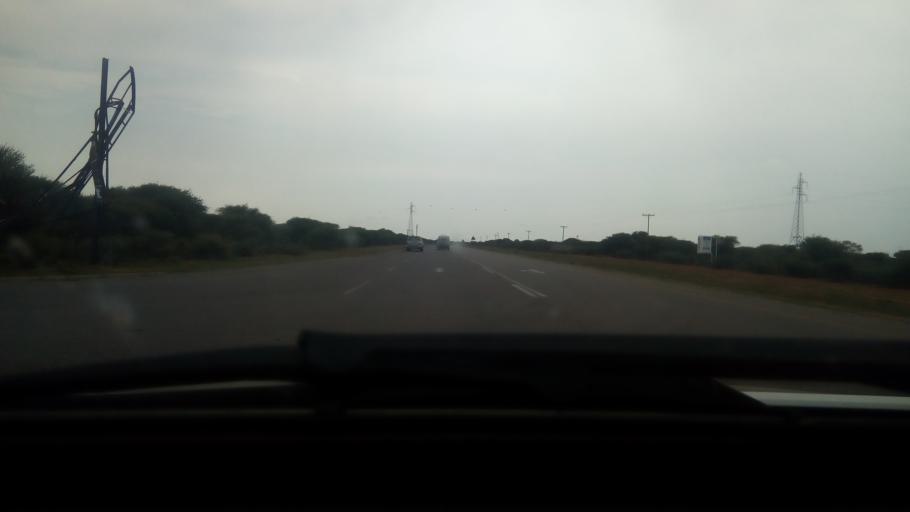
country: BW
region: South East
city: Gaborone
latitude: -24.6713
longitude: 26.0353
